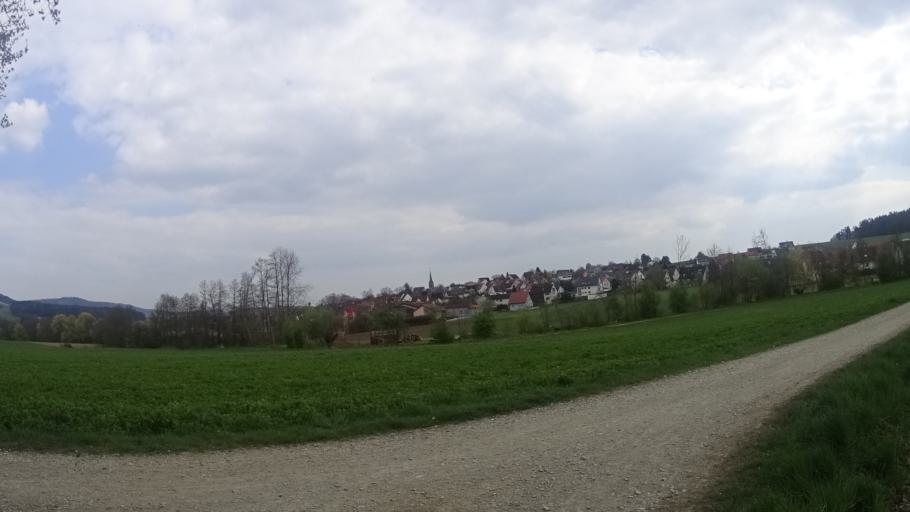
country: DE
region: Bavaria
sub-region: Upper Franconia
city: Igensdorf
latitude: 49.6187
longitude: 11.2200
